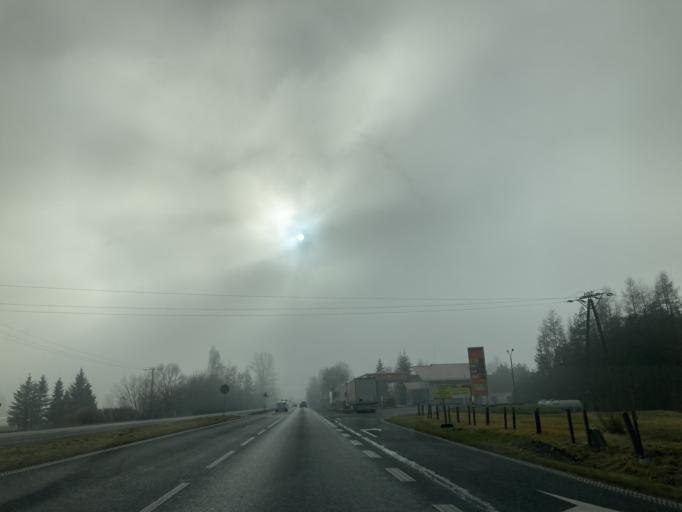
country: PL
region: Silesian Voivodeship
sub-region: Powiat cieszynski
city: Gorki Wielkie
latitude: 49.7763
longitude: 18.8087
